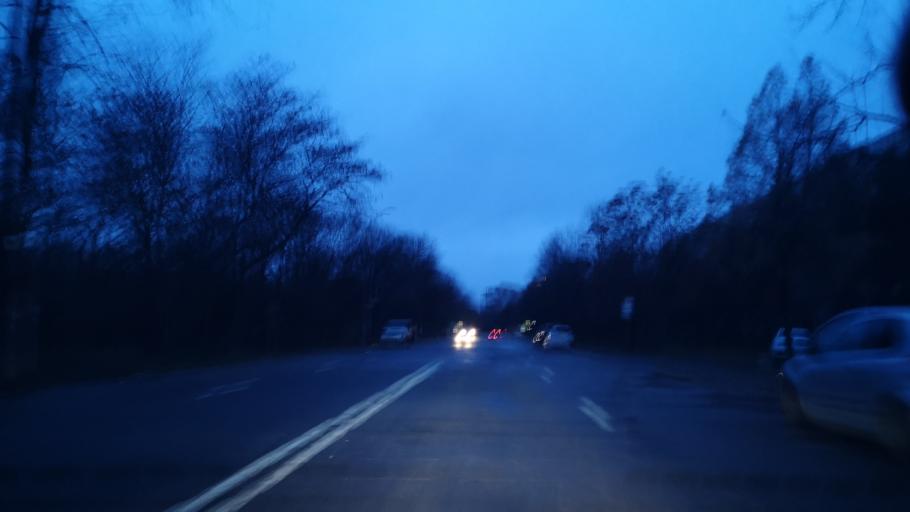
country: MD
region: Chisinau
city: Chisinau
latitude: 47.0354
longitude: 28.8784
